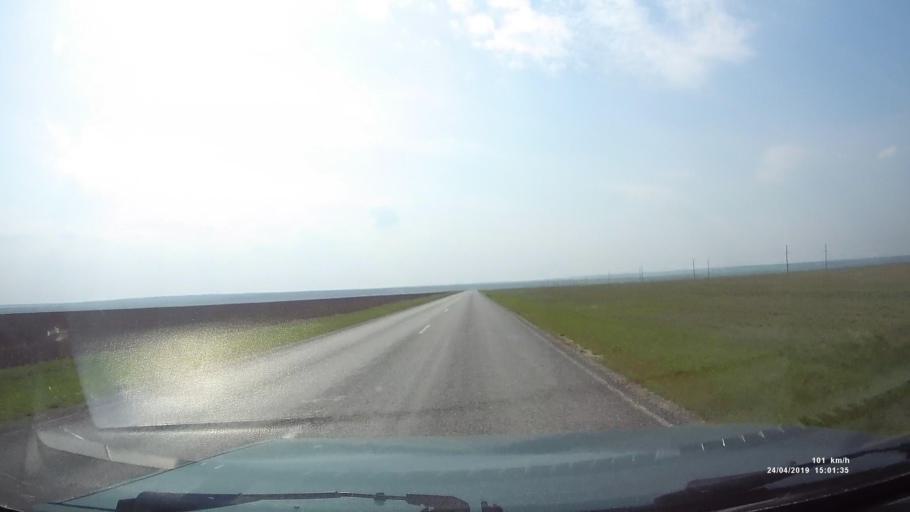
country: RU
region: Rostov
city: Remontnoye
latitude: 46.5662
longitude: 43.5310
